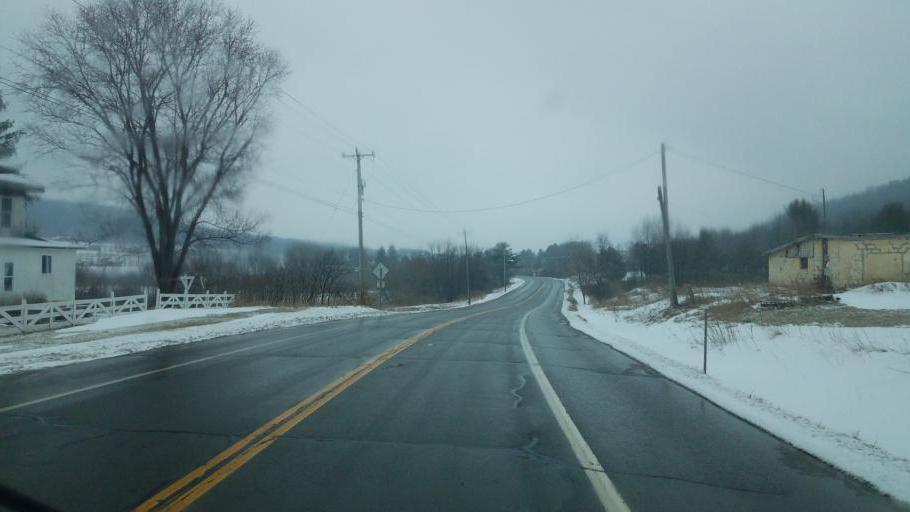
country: US
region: Pennsylvania
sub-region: Tioga County
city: Westfield
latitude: 42.1113
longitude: -77.4850
